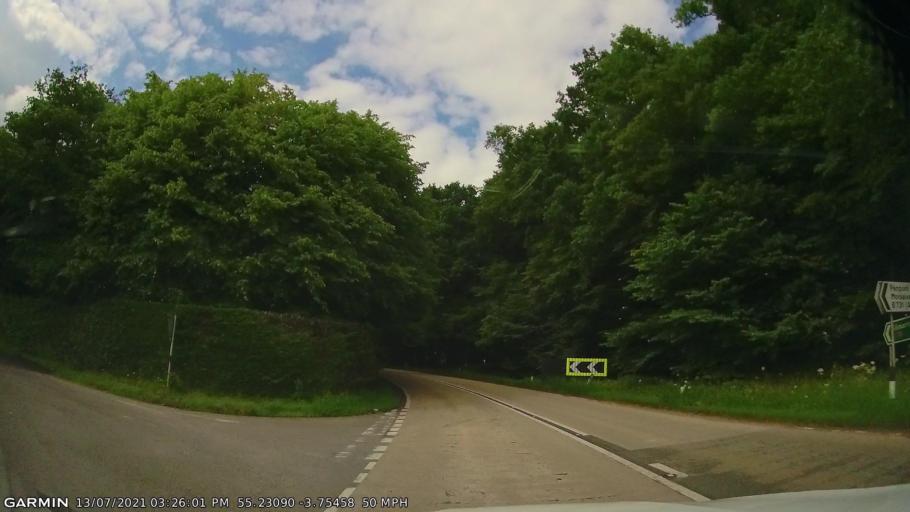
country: GB
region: Scotland
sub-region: Dumfries and Galloway
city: Thornhill
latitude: 55.2309
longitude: -3.7546
